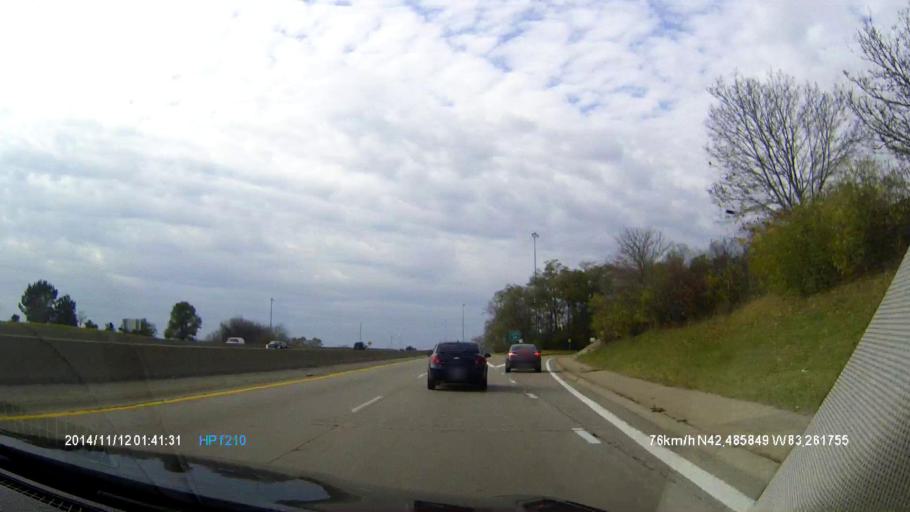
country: US
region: Michigan
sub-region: Oakland County
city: Bingham Farms
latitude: 42.4858
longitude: -83.2617
